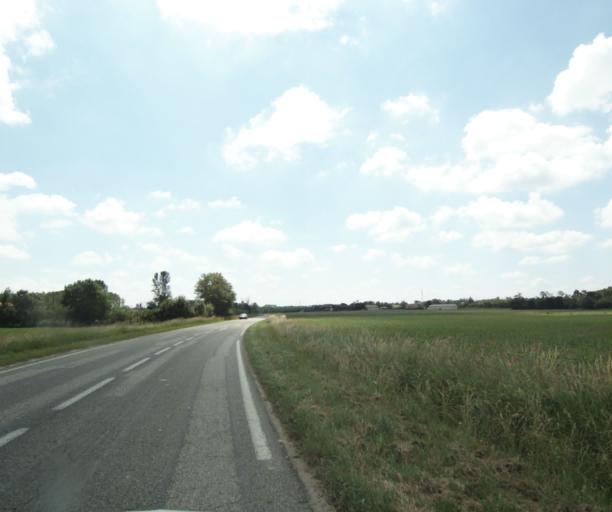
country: FR
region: Midi-Pyrenees
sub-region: Departement du Tarn-et-Garonne
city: Montauban
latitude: 44.0645
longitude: 1.3590
